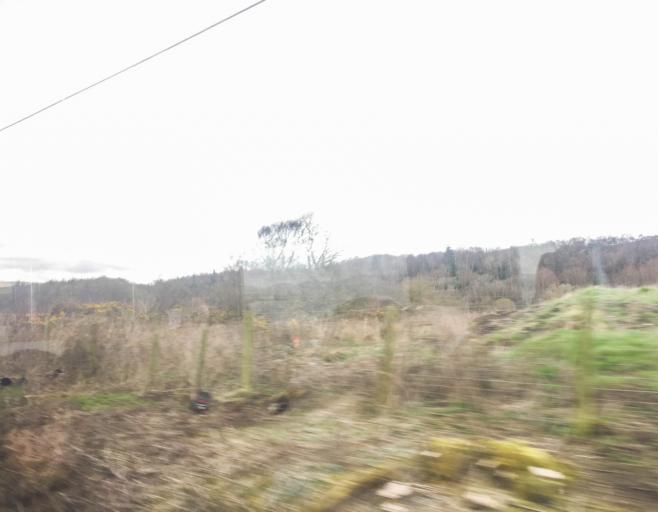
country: GB
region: Scotland
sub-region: Argyll and Bute
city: Helensburgh
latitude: 55.9883
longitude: -4.6963
